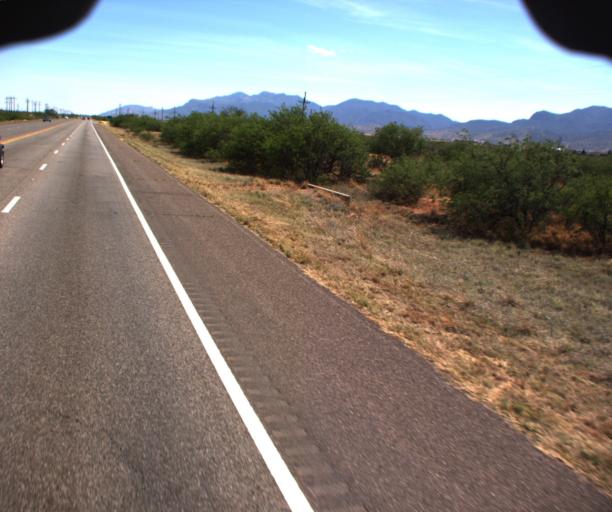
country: US
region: Arizona
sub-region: Cochise County
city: Huachuca City
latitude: 31.5981
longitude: -110.3264
